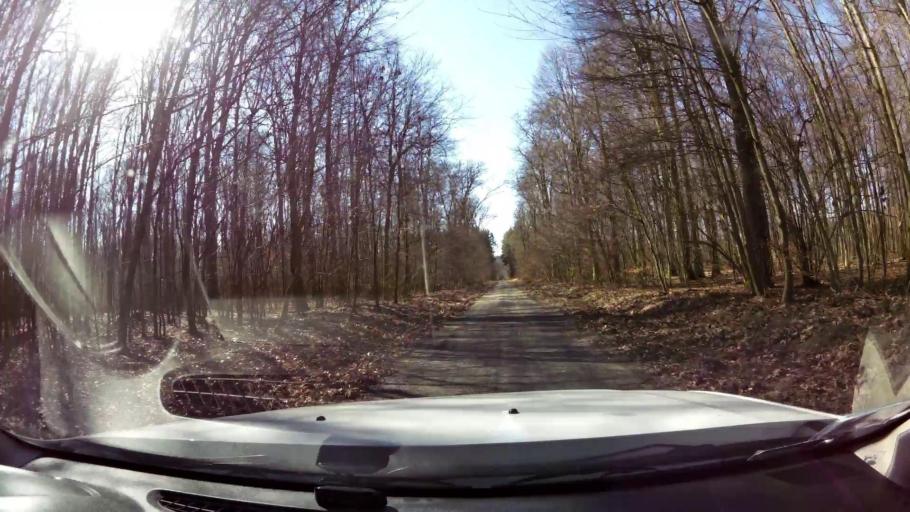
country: PL
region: West Pomeranian Voivodeship
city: Trzcinsko Zdroj
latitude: 53.0200
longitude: 14.6327
